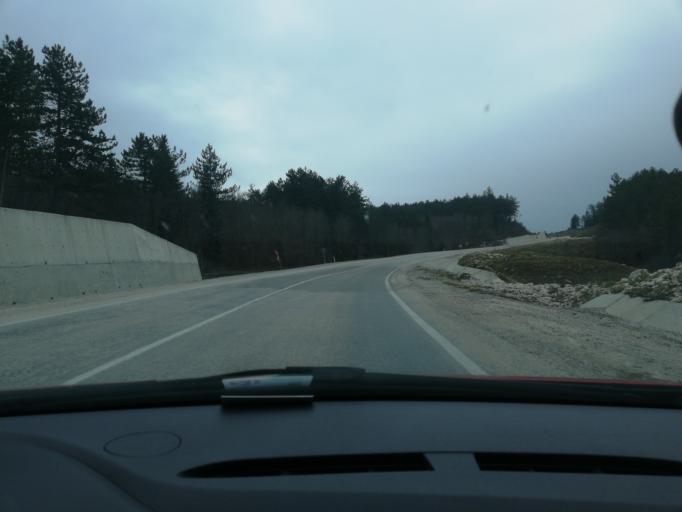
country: TR
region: Kastamonu
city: Pinarbasi
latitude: 41.5715
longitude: 33.0988
